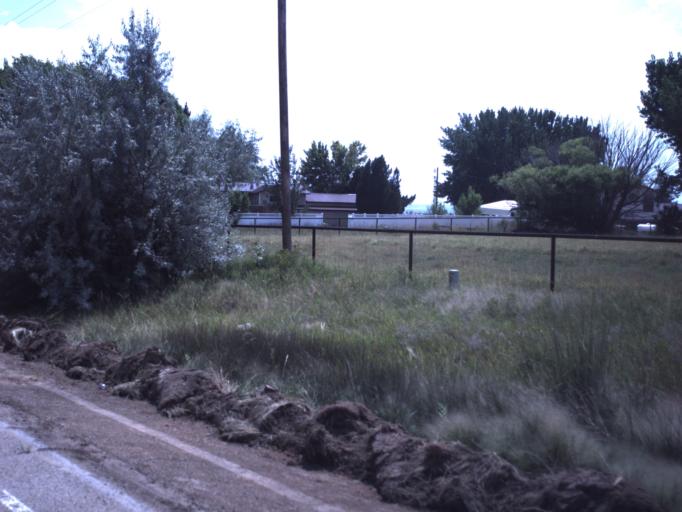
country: US
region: Utah
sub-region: Duchesne County
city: Roosevelt
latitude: 40.3469
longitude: -110.0281
